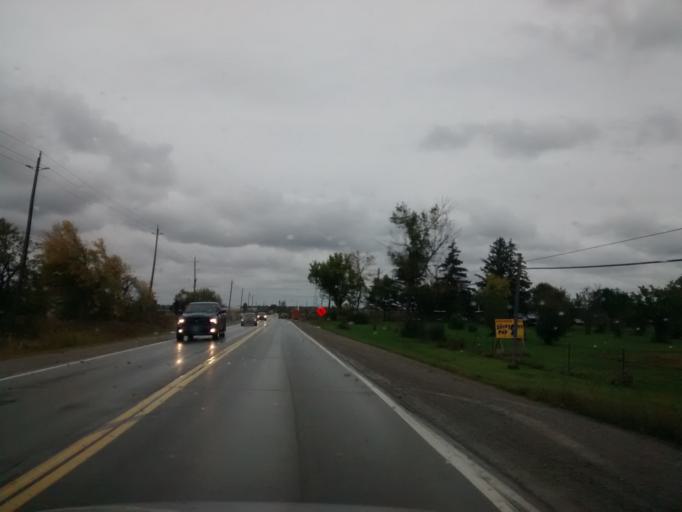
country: CA
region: Ontario
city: Hamilton
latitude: 43.1634
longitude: -79.7862
